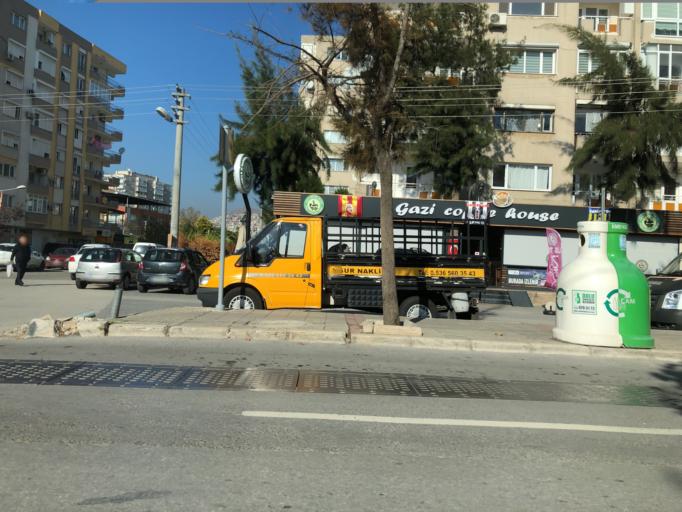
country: TR
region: Izmir
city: Bornova
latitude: 38.4578
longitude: 27.1866
